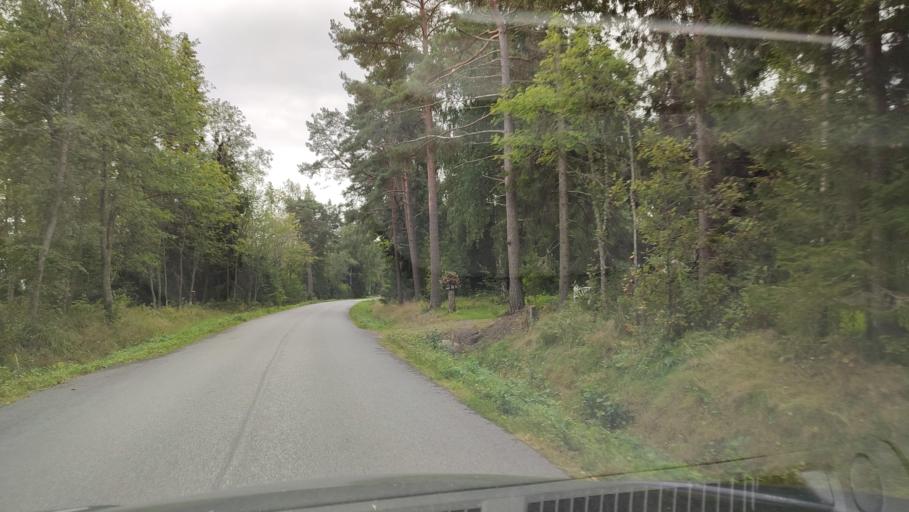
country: FI
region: Ostrobothnia
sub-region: Sydosterbotten
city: Kristinestad
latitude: 62.2563
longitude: 21.3564
